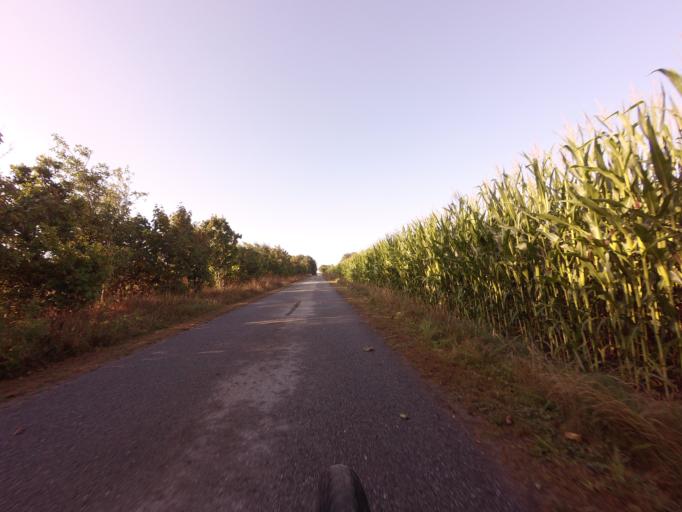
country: DK
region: North Denmark
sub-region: Hjorring Kommune
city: Vra
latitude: 57.3649
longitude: 9.8652
